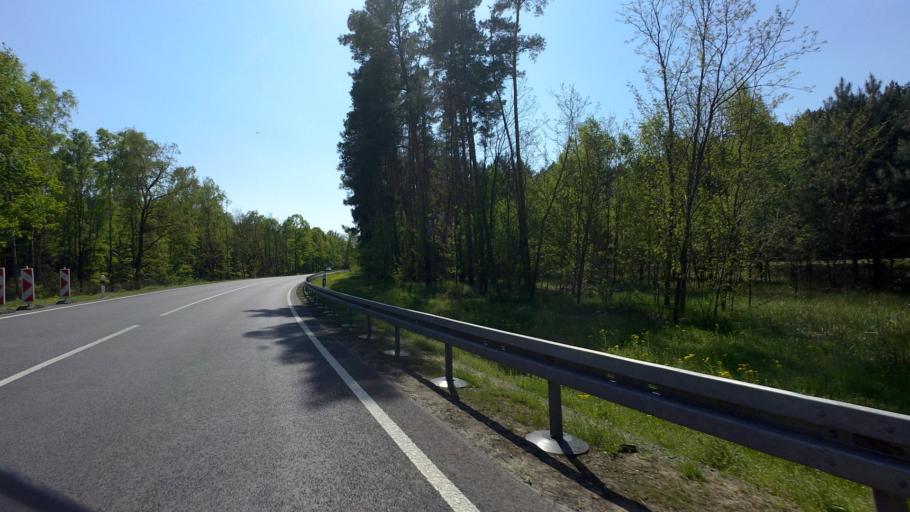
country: DE
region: Brandenburg
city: Beeskow
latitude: 52.1492
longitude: 14.2137
